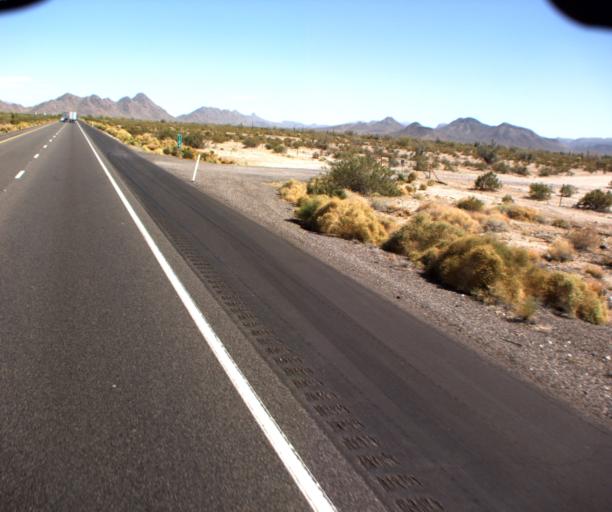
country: US
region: Arizona
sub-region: Maricopa County
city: Gila Bend
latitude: 32.9085
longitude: -112.5956
